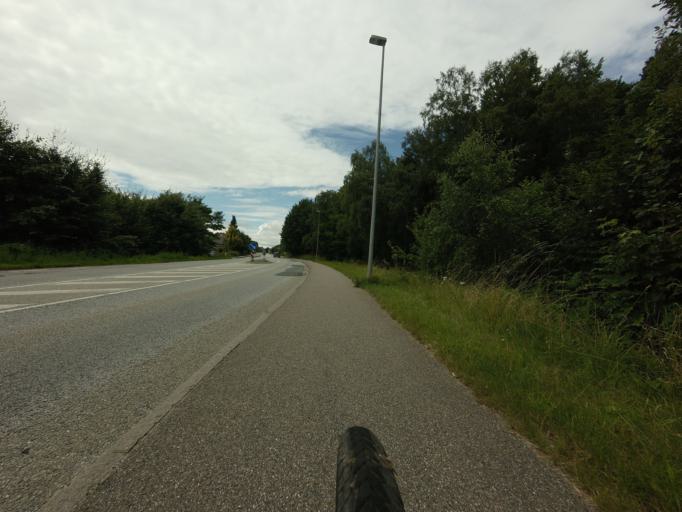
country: DK
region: Central Jutland
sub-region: Syddjurs Kommune
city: Ryomgard
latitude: 56.3796
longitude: 10.5135
